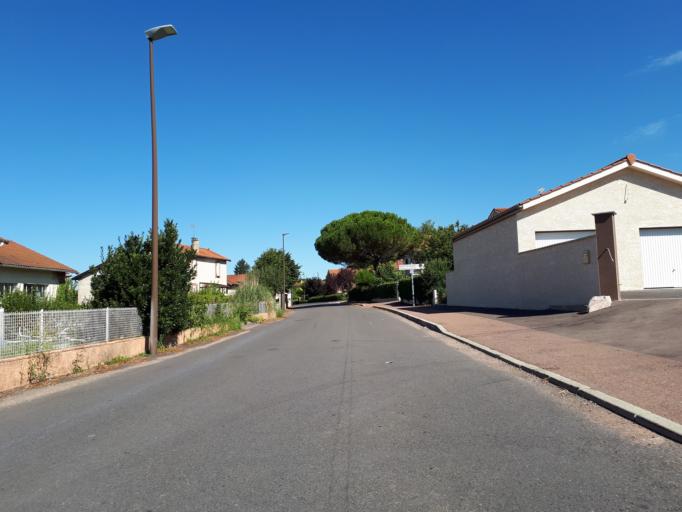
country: FR
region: Rhone-Alpes
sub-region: Departement de la Loire
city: Pouilly-les-Feurs
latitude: 45.7960
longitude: 4.2351
